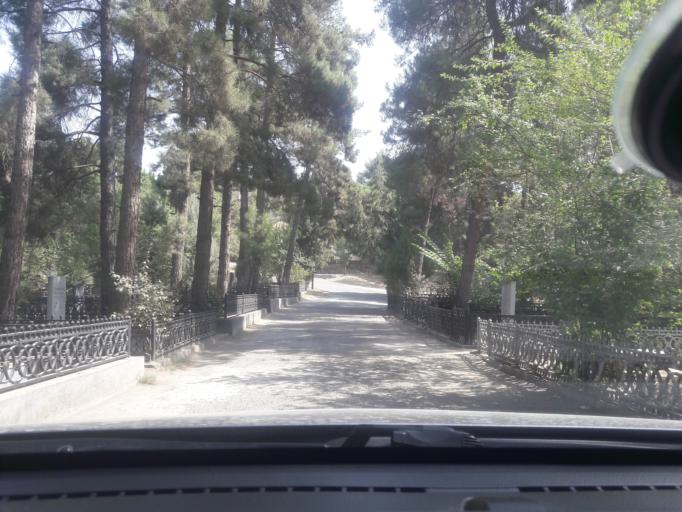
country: TJ
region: Dushanbe
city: Dushanbe
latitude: 38.6023
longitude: 68.7974
